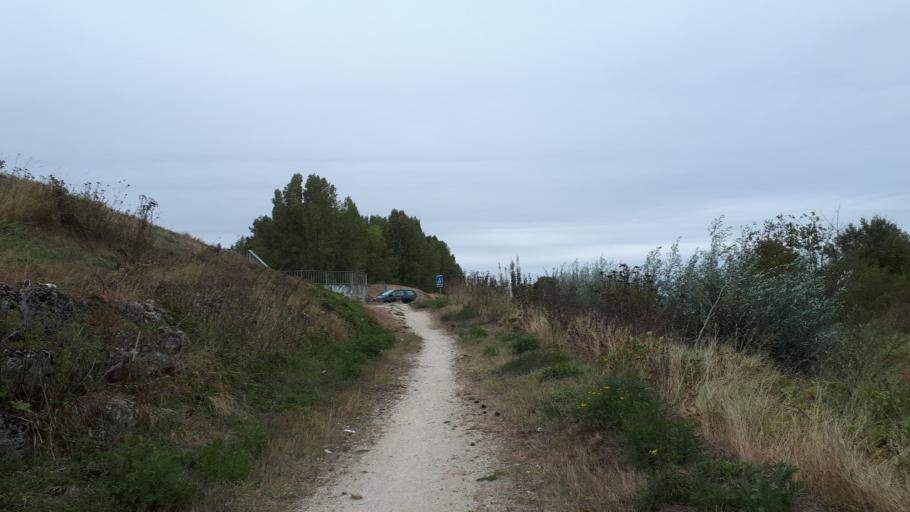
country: FR
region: Centre
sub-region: Departement du Loir-et-Cher
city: Saint-Gervais-la-Foret
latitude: 47.5692
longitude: 1.3405
